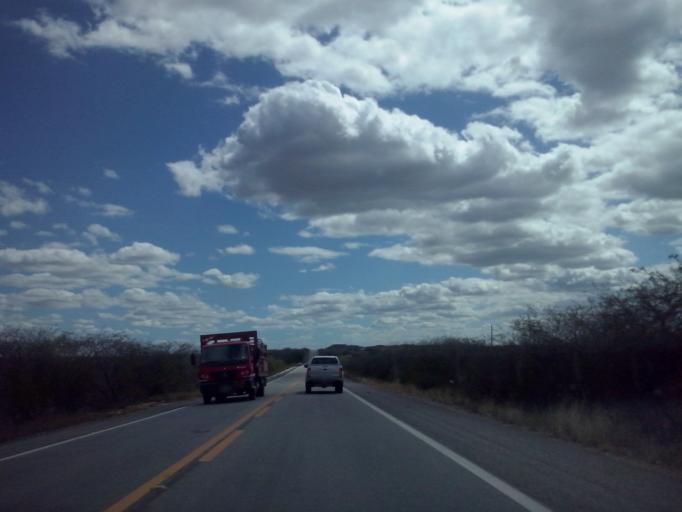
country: BR
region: Paraiba
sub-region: Soledade
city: Soledade
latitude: -7.0380
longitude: -36.4326
